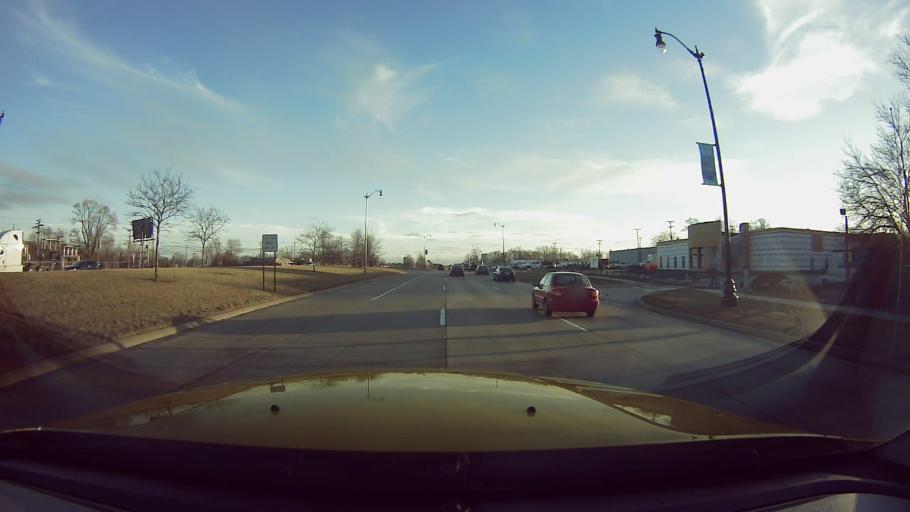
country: US
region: Michigan
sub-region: Wayne County
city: Taylor
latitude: 42.2211
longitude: -83.2692
